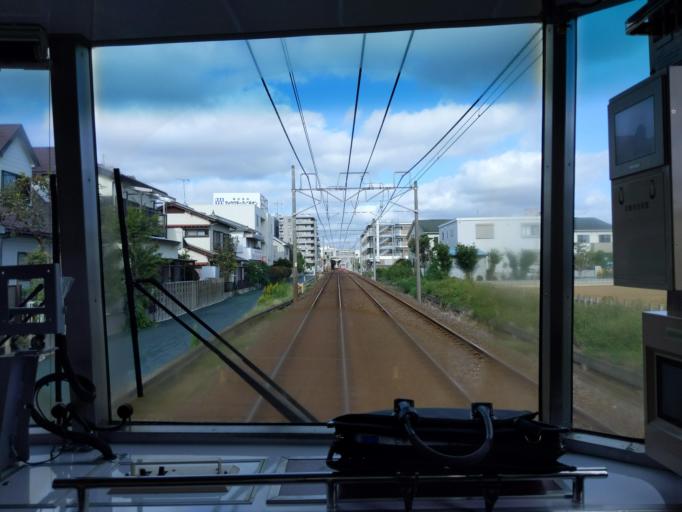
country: JP
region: Chiba
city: Funabashi
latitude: 35.7078
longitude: 140.0352
